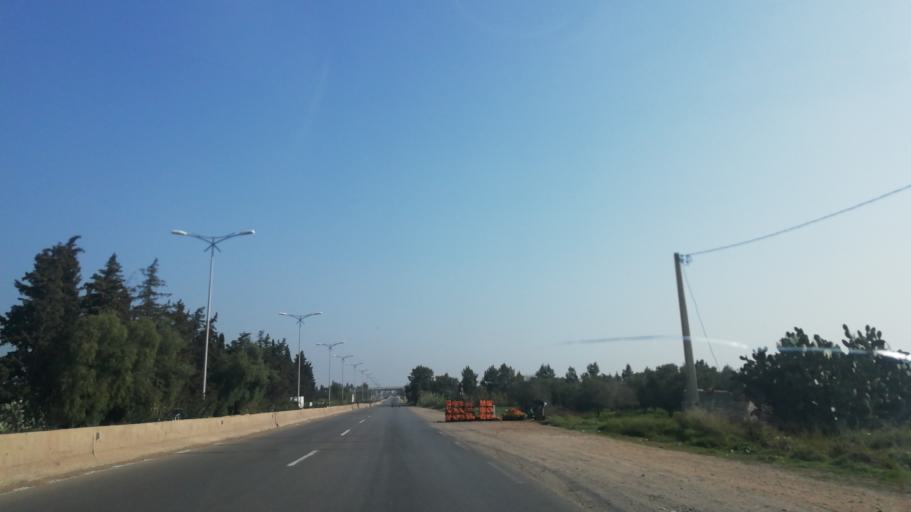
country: DZ
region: Oran
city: Bou Tlelis
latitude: 35.5728
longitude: -0.8732
